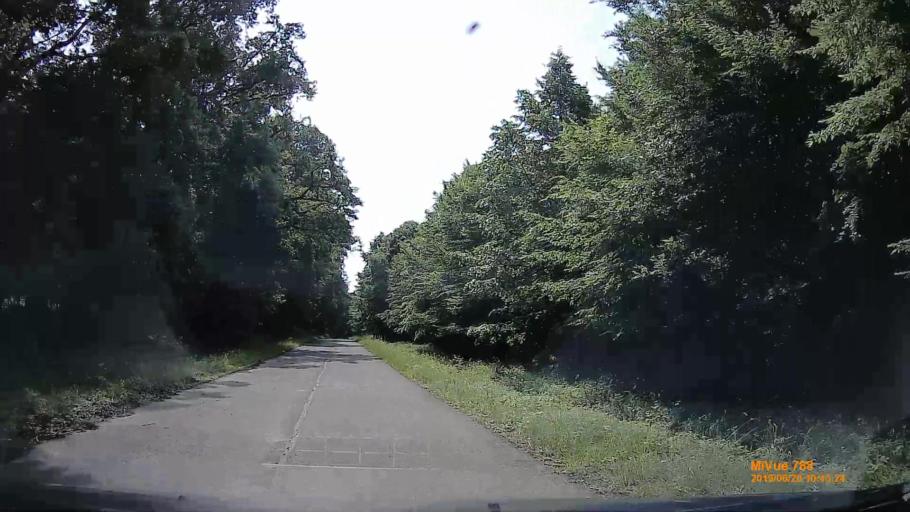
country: HU
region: Baranya
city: Hidas
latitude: 46.1831
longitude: 18.5708
